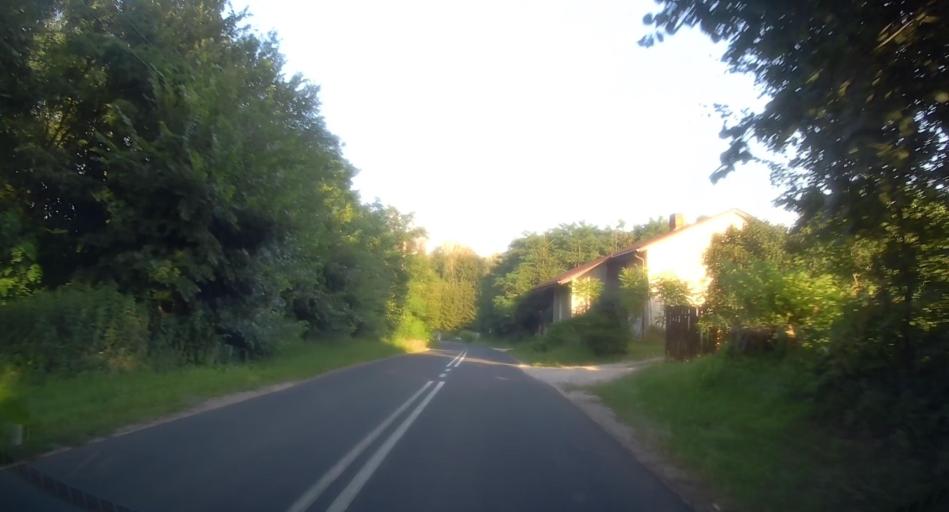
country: PL
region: Lodz Voivodeship
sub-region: Powiat skierniewicki
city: Kowiesy
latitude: 51.8973
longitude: 20.3760
